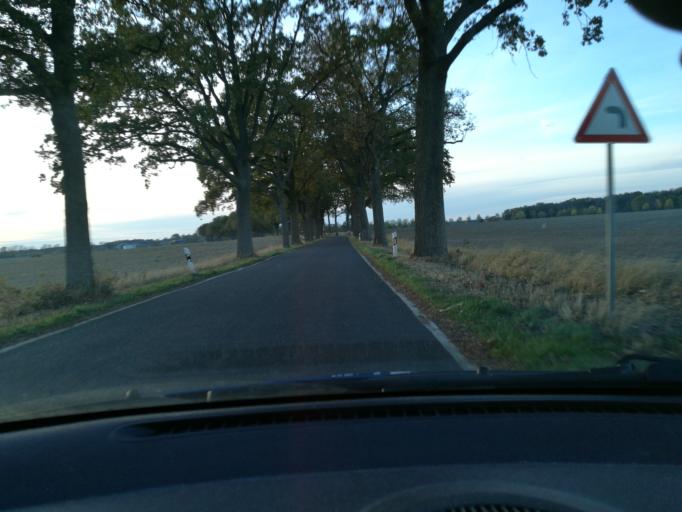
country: DE
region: Brandenburg
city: Karstadt
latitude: 53.0967
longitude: 11.7125
